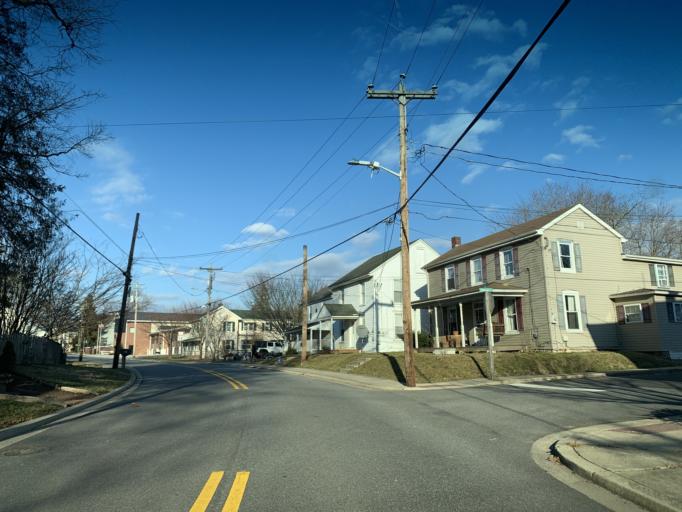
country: US
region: Maryland
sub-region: Queen Anne's County
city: Kingstown
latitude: 39.1408
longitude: -75.9867
